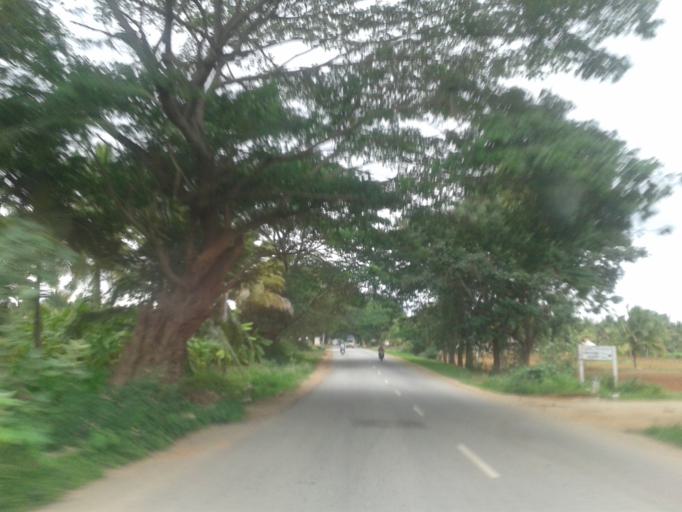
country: IN
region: Karnataka
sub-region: Hassan
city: Shravanabelagola
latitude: 12.8730
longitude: 76.4464
